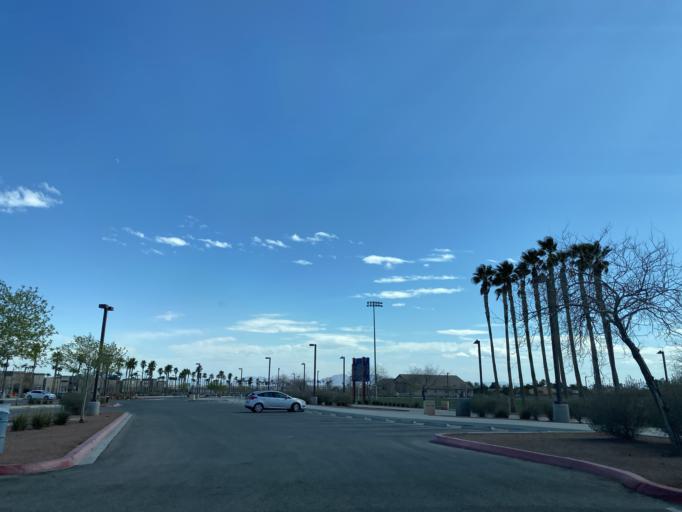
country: US
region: Nevada
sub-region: Clark County
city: Summerlin South
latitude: 36.2734
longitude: -115.2849
